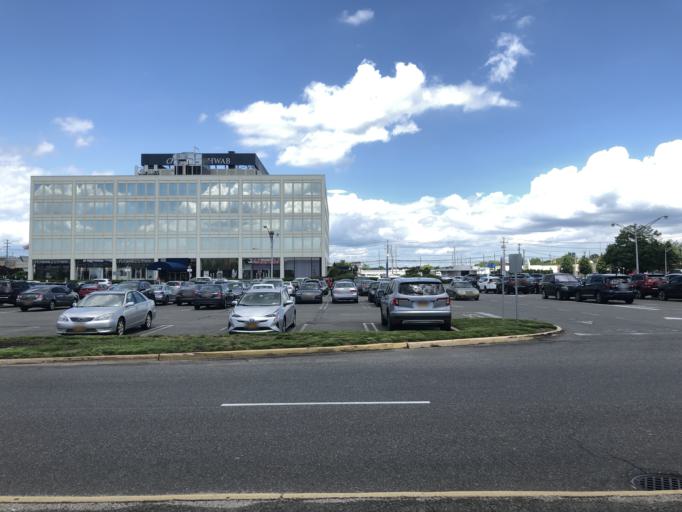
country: US
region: New York
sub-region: Nassau County
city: Carle Place
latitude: 40.7415
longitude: -73.6149
